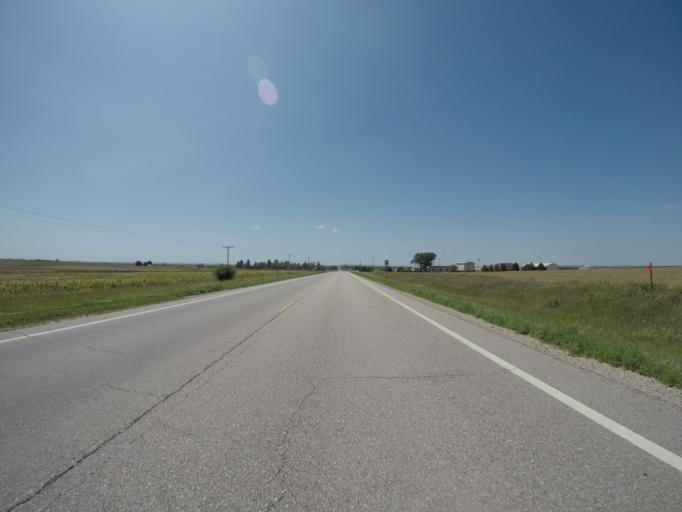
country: US
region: Kansas
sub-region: Osborne County
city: Osborne
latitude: 39.4577
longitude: -98.6947
